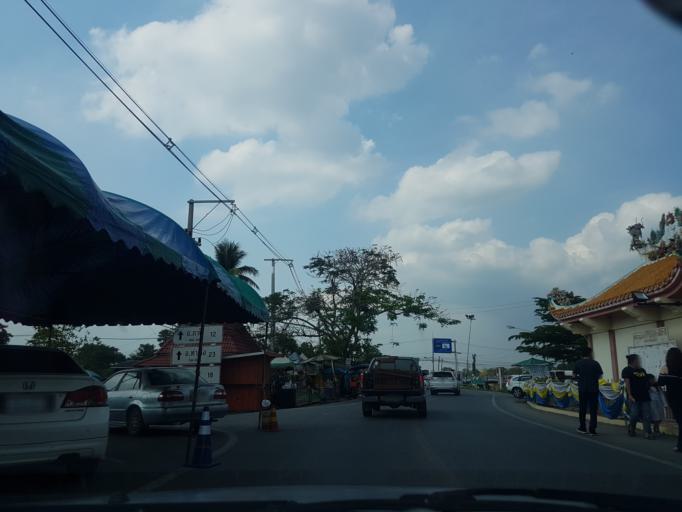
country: TH
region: Phra Nakhon Si Ayutthaya
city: Phachi
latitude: 14.3968
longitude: 100.7931
